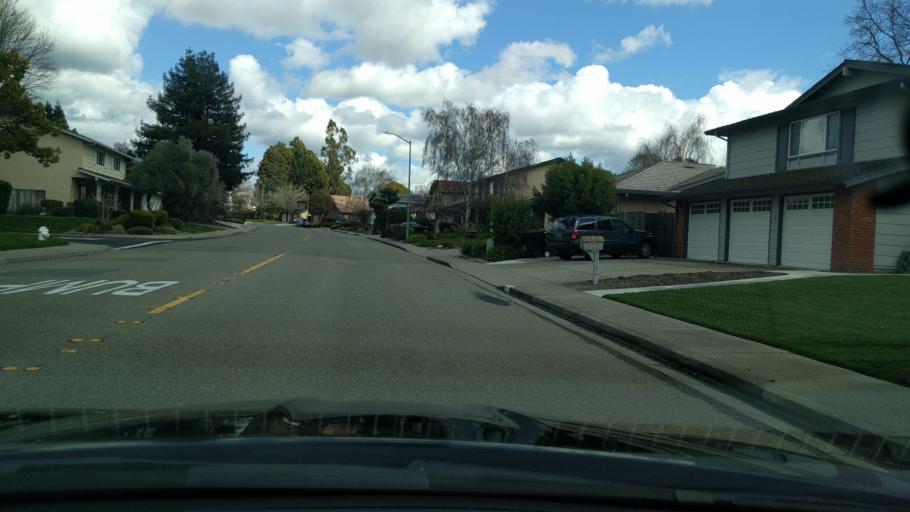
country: US
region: California
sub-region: Contra Costa County
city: San Ramon
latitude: 37.7608
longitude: -121.9777
